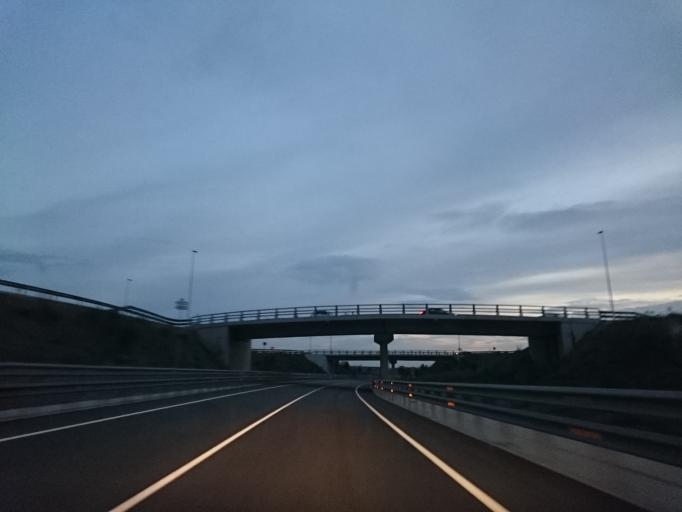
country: ES
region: Catalonia
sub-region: Provincia de Barcelona
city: Vilafranca del Penedes
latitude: 41.3516
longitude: 1.7223
